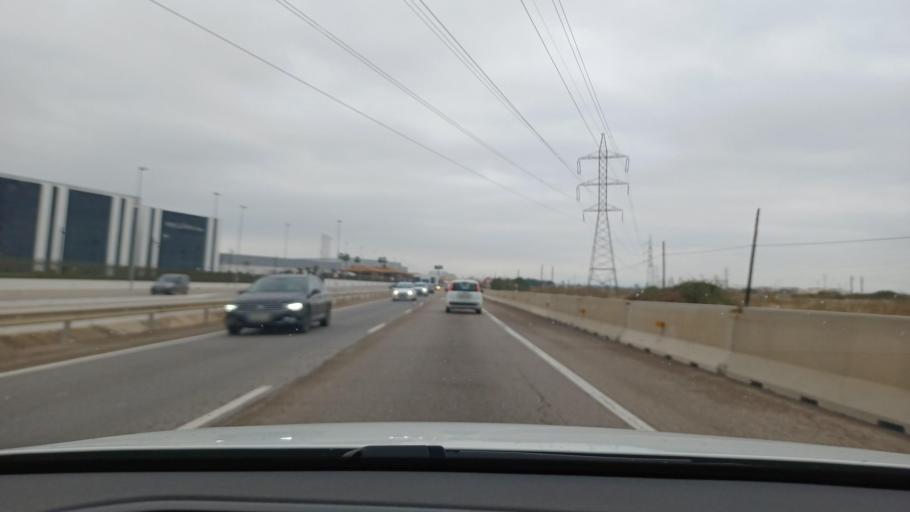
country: ES
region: Valencia
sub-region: Provincia de Castello
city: Vila-real
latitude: 39.9161
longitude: -0.1112
